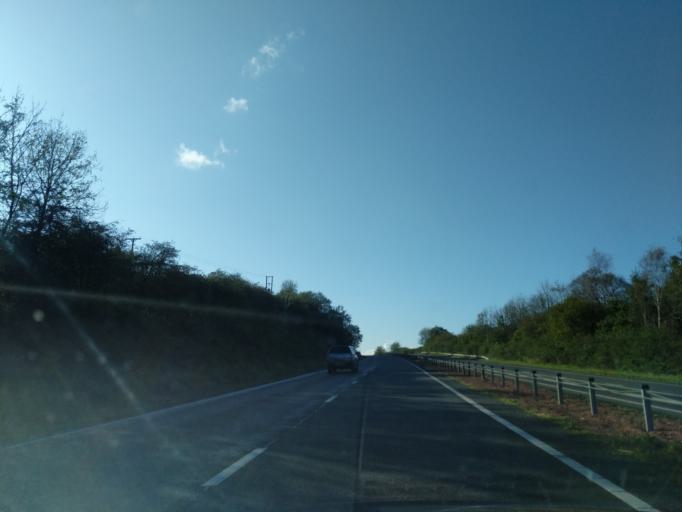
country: GB
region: Scotland
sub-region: Dumfries and Galloway
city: Dumfries
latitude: 55.0584
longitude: -3.7024
